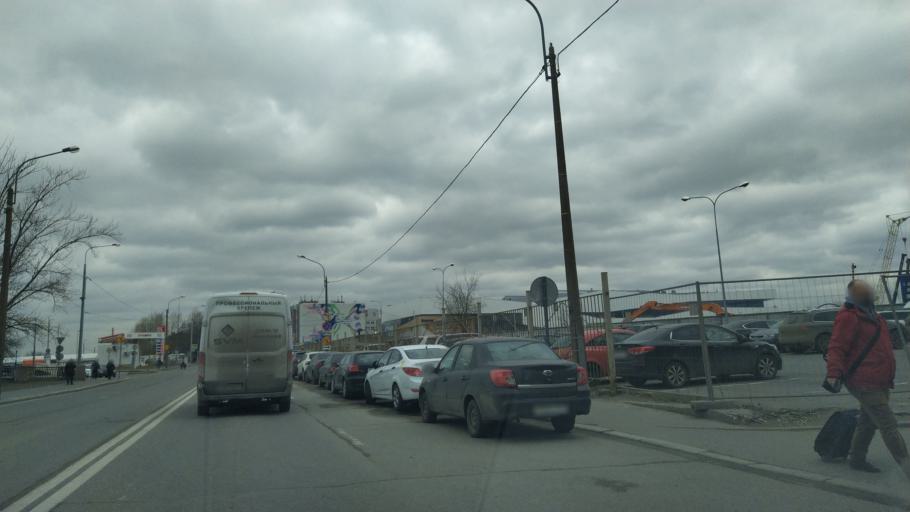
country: RU
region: St.-Petersburg
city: Centralniy
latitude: 59.9363
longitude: 30.4162
